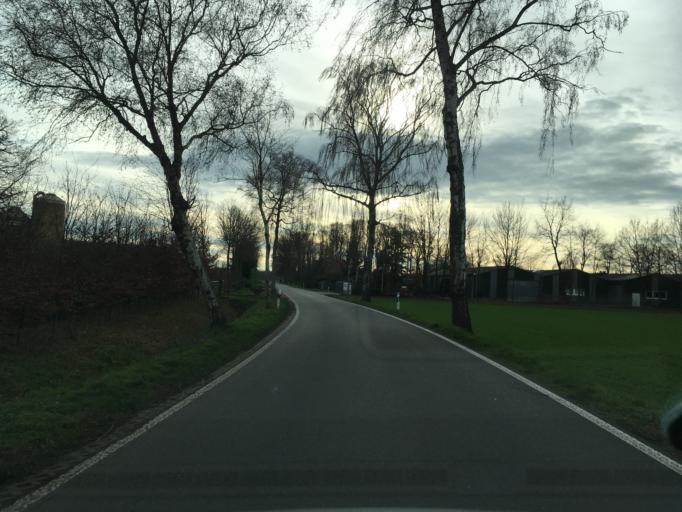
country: DE
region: North Rhine-Westphalia
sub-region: Regierungsbezirk Munster
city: Legden
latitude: 52.0685
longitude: 7.0987
